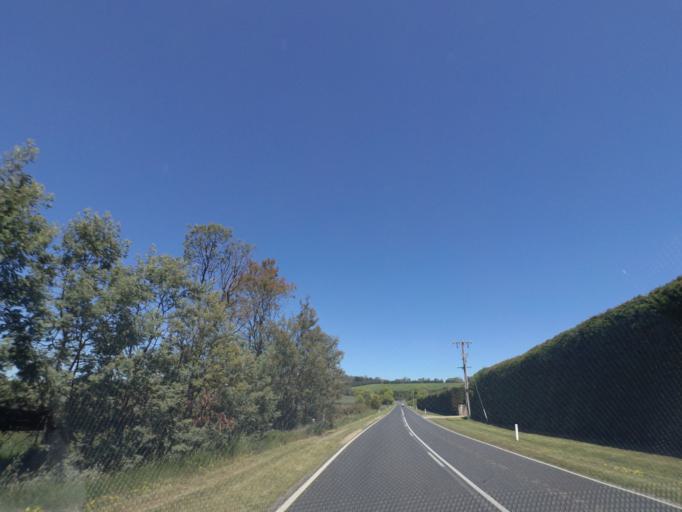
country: AU
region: Victoria
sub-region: Hume
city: Sunbury
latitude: -37.2963
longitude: 144.6927
